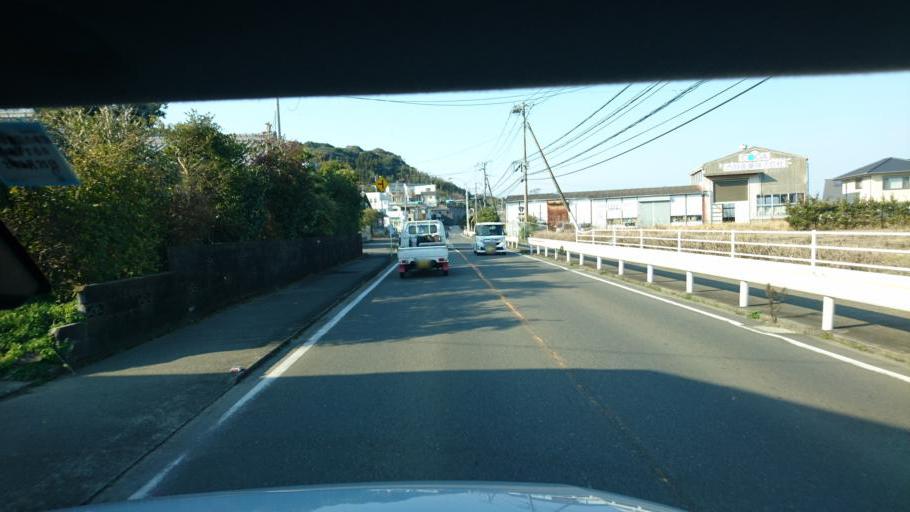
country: JP
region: Miyazaki
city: Miyazaki-shi
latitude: 31.9779
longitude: 131.4400
